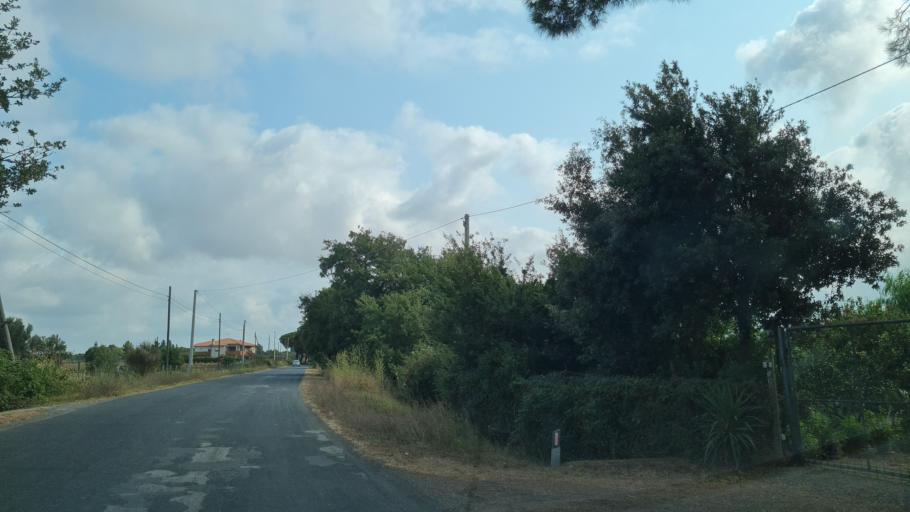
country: IT
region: Latium
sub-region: Provincia di Viterbo
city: Montalto di Castro
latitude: 42.3187
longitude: 11.6107
